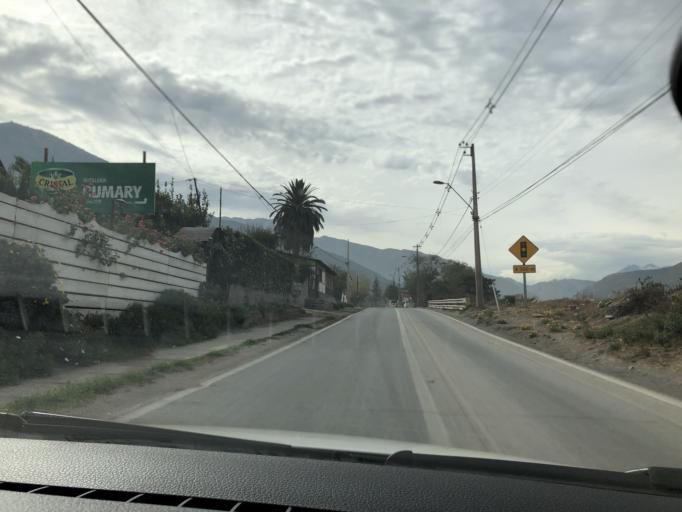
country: CL
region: Santiago Metropolitan
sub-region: Provincia de Cordillera
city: Puente Alto
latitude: -33.5943
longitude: -70.4895
